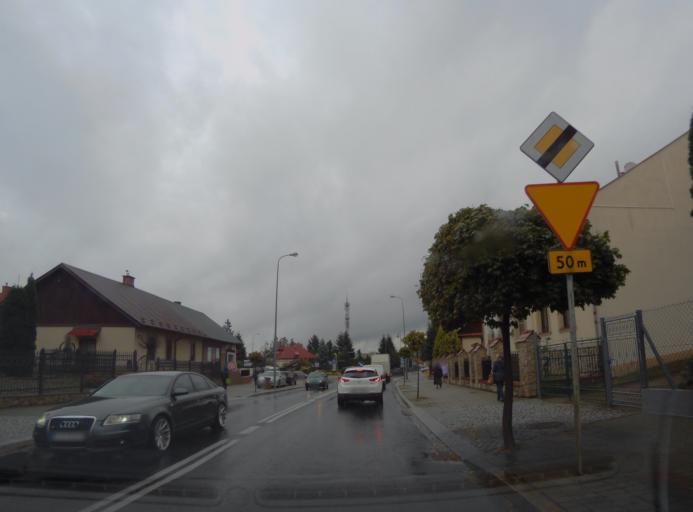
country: PL
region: Subcarpathian Voivodeship
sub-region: Powiat lezajski
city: Lezajsk
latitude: 50.2565
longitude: 22.4216
